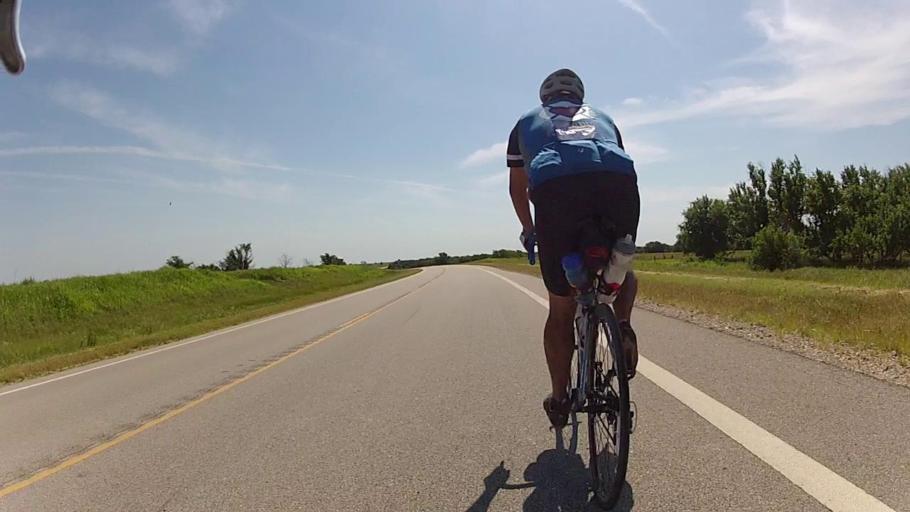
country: US
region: Kansas
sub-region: Chautauqua County
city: Sedan
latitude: 37.1068
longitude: -96.5413
